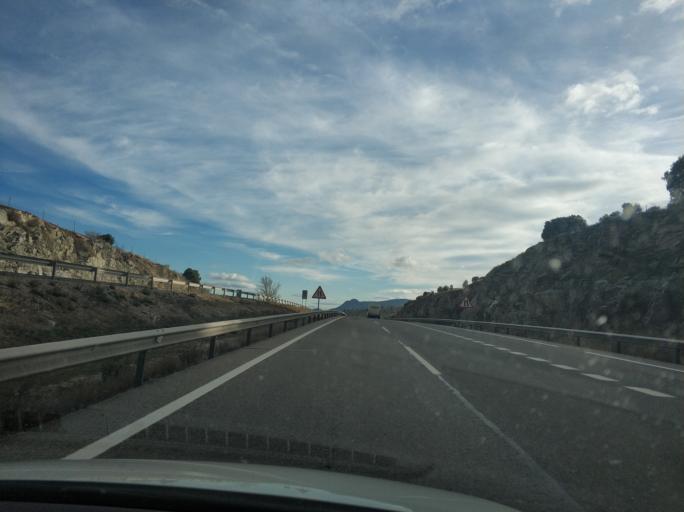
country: ES
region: Madrid
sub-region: Provincia de Madrid
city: Buitrago del Lozoya
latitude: 40.9559
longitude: -3.6412
